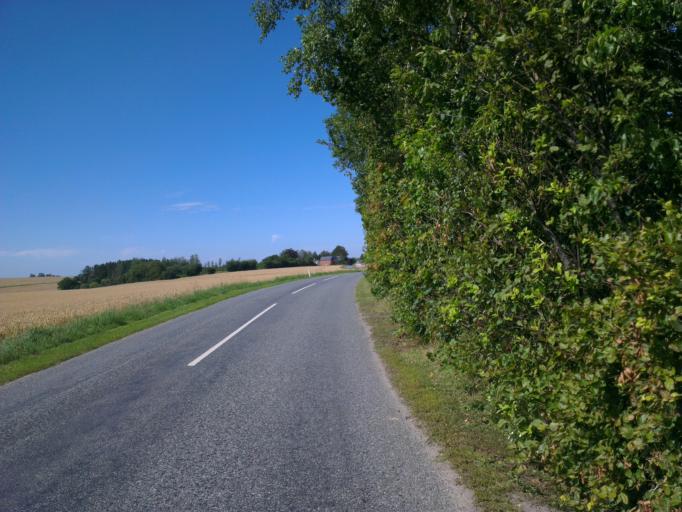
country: DK
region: Capital Region
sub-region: Frederikssund Kommune
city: Frederikssund
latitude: 55.8665
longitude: 12.0910
